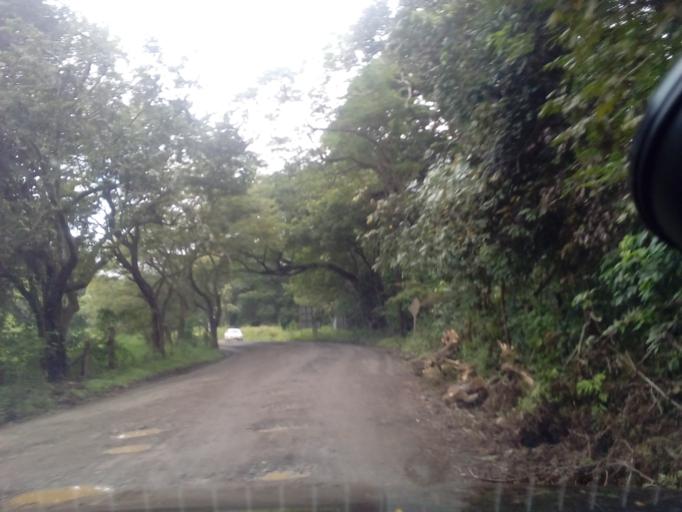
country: CR
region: Guanacaste
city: Samara
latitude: 9.9302
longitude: -85.6534
